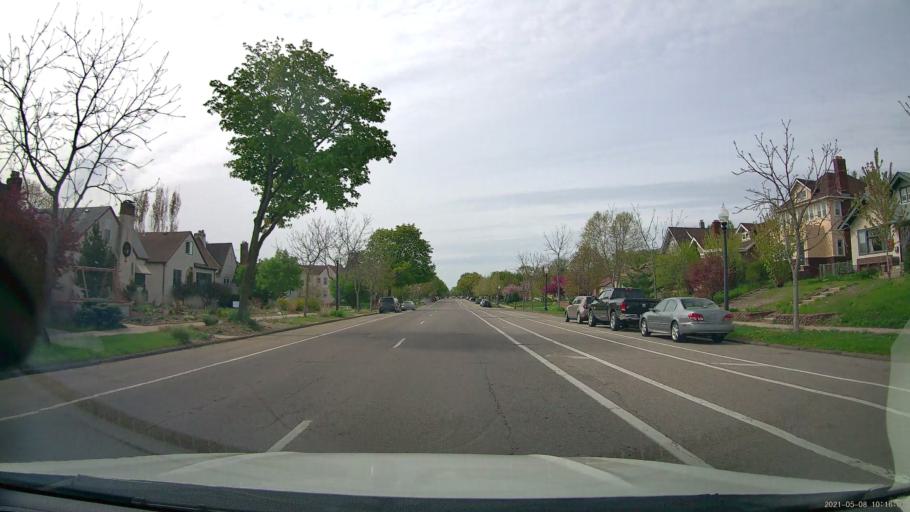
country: US
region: Minnesota
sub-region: Hennepin County
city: Richfield
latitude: 44.9240
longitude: -93.2676
